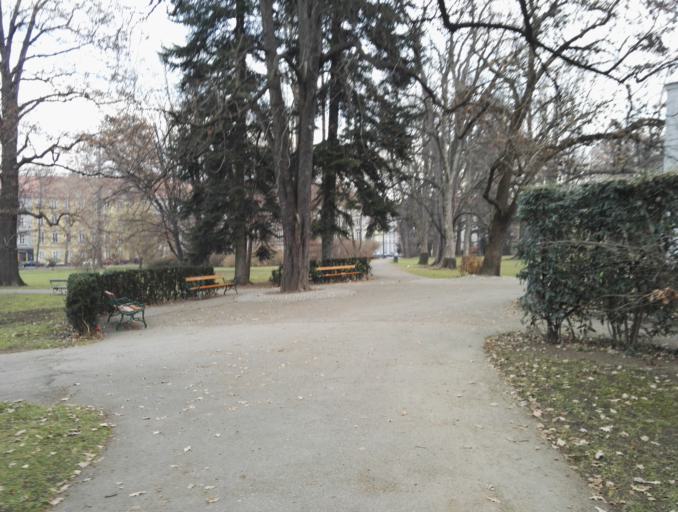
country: AT
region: Styria
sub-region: Graz Stadt
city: Graz
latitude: 47.0767
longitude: 15.4425
